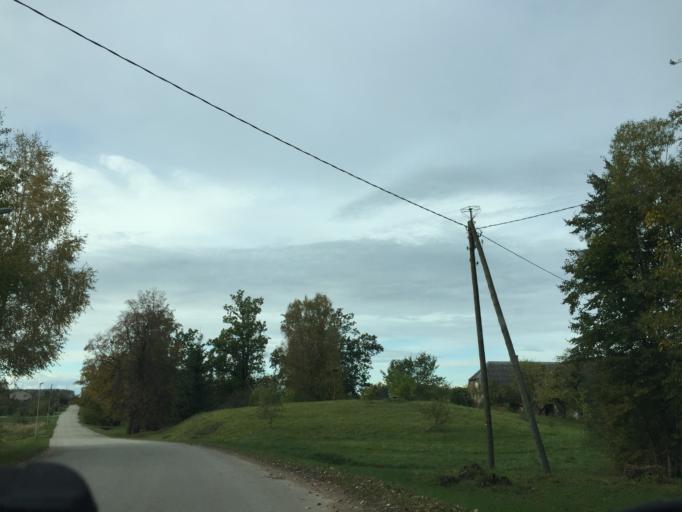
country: LV
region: Auces Novads
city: Auce
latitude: 56.5425
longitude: 22.9951
